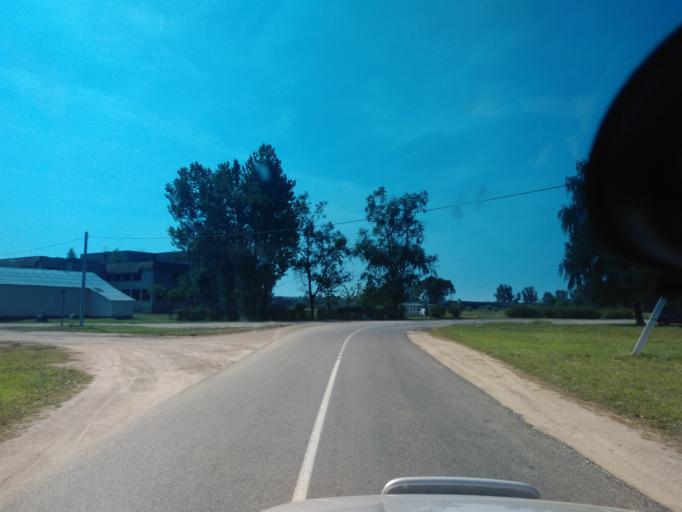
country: BY
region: Minsk
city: Kapyl'
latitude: 53.2596
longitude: 27.1892
